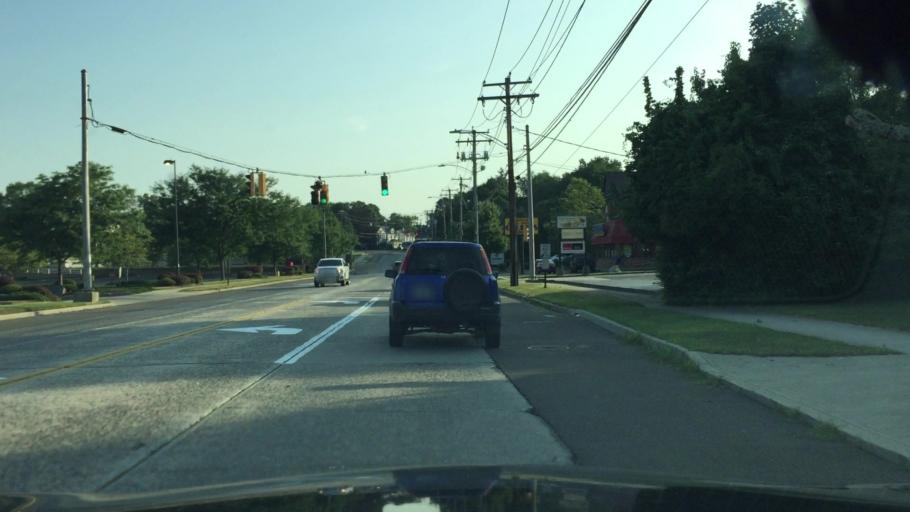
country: US
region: Connecticut
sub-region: New Haven County
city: Milford
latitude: 41.2292
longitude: -73.0490
